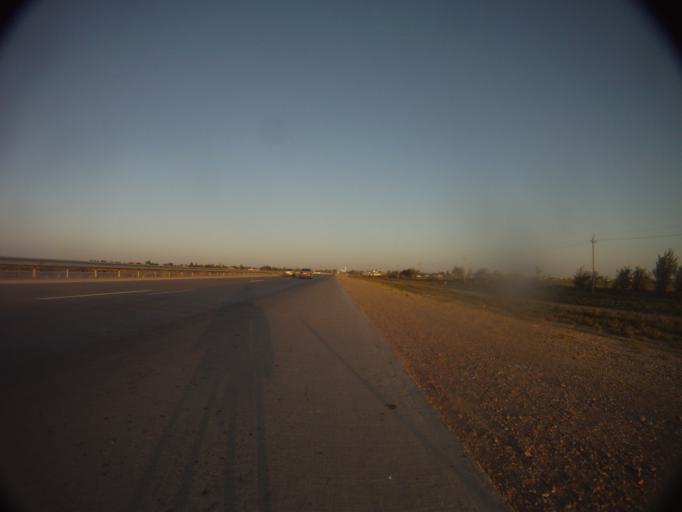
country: KZ
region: Ongtustik Qazaqstan
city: Turkestan
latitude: 43.2659
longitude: 68.3622
